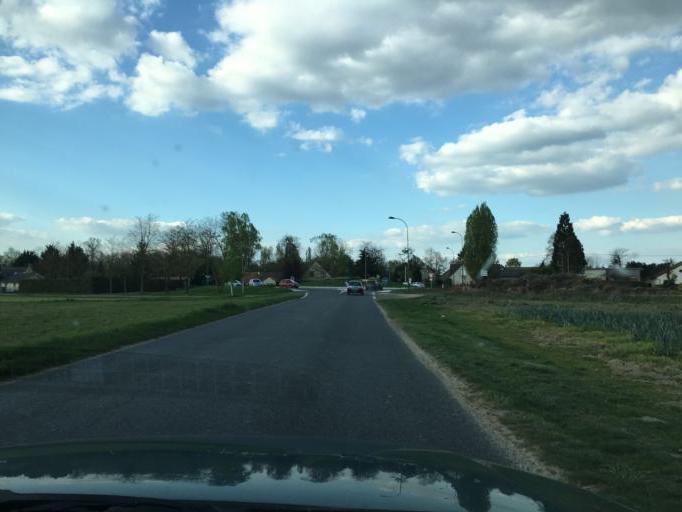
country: FR
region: Centre
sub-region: Departement du Loiret
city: Saint-Denis-en-Val
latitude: 47.8672
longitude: 1.9574
